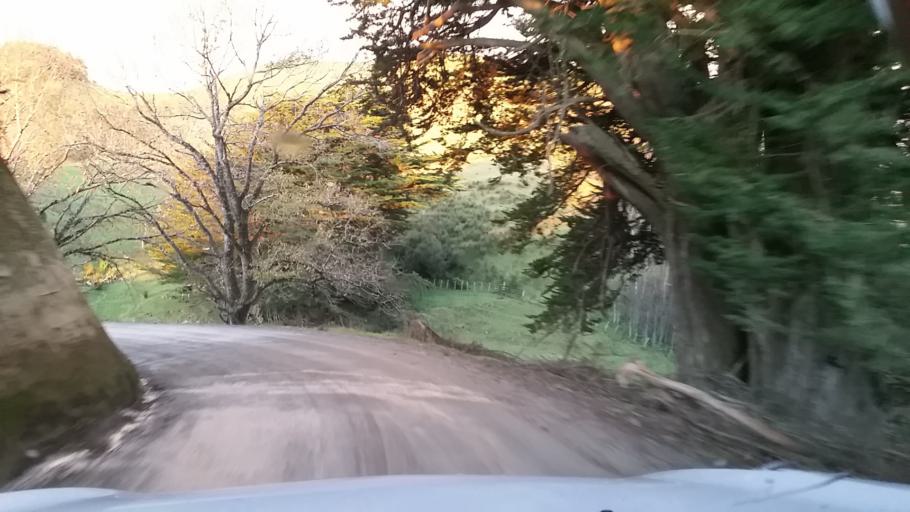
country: NZ
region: Manawatu-Wanganui
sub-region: Wanganui District
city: Wanganui
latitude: -39.7667
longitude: 174.8716
